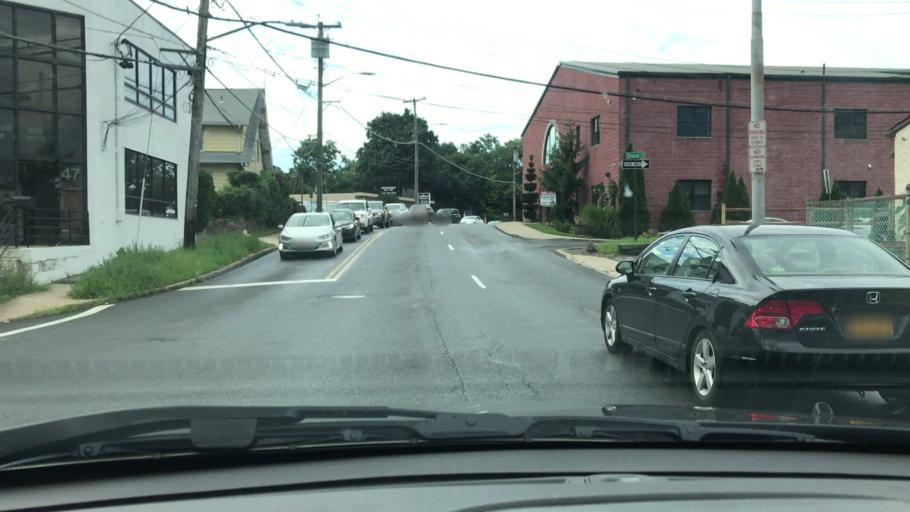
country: US
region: New York
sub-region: Westchester County
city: New Rochelle
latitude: 40.9264
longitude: -73.7728
